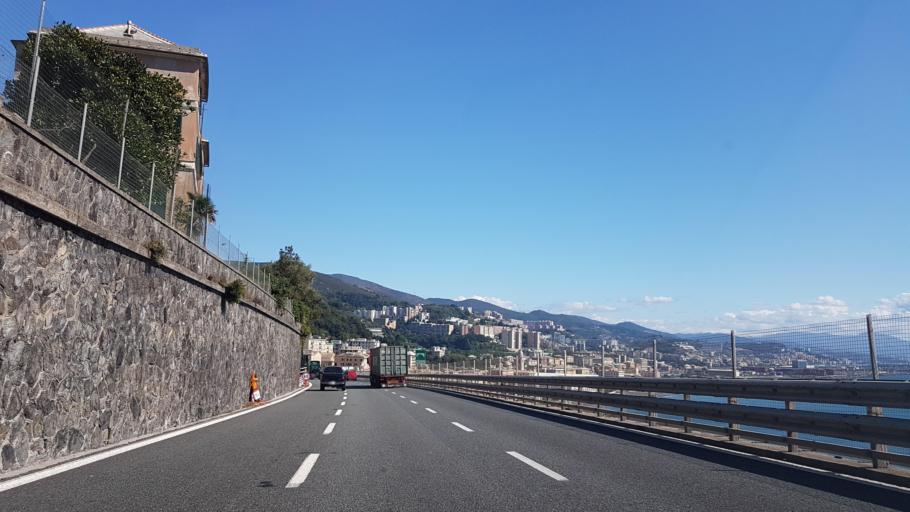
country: IT
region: Liguria
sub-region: Provincia di Genova
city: Mele
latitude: 44.4263
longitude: 8.7388
